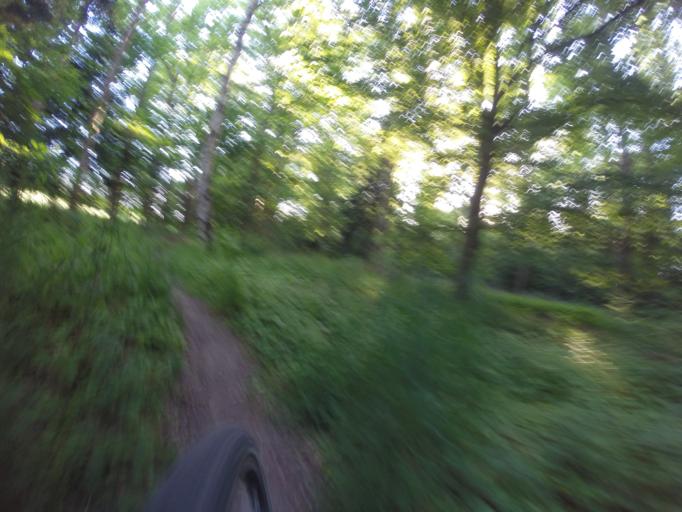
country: DK
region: Capital Region
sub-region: Hoje-Taastrup Kommune
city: Taastrup
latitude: 55.6830
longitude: 12.3128
